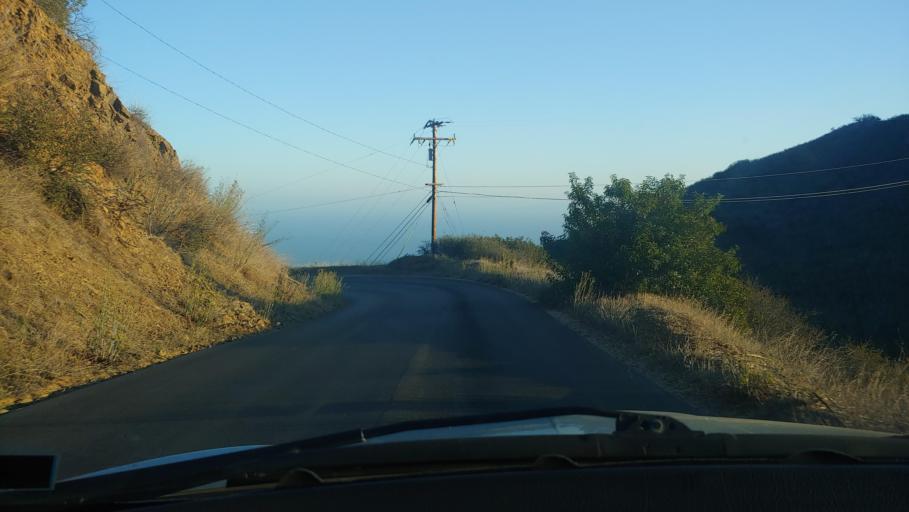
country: US
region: California
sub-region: Santa Barbara County
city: Mission Canyon
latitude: 34.4681
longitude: -119.6772
